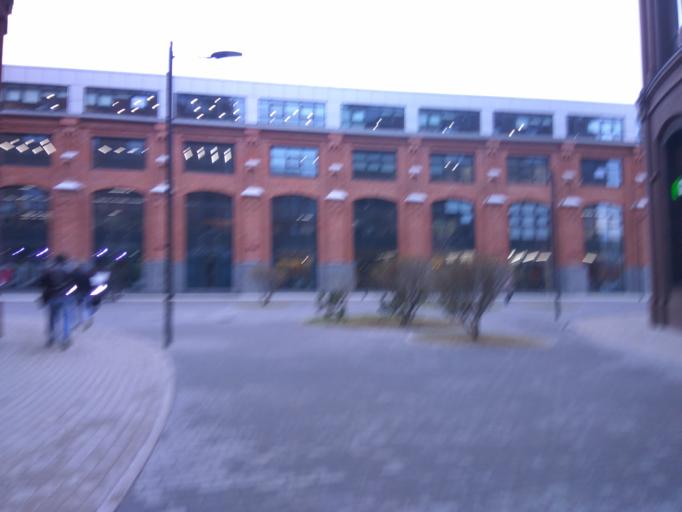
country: RU
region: Moscow
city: Taganskiy
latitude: 55.7595
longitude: 37.6650
